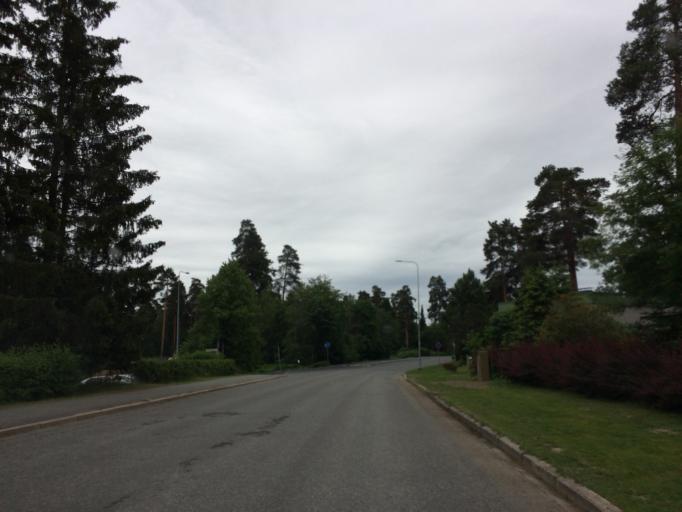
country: FI
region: Haeme
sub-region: Haemeenlinna
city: Haemeenlinna
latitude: 61.0113
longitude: 24.4982
